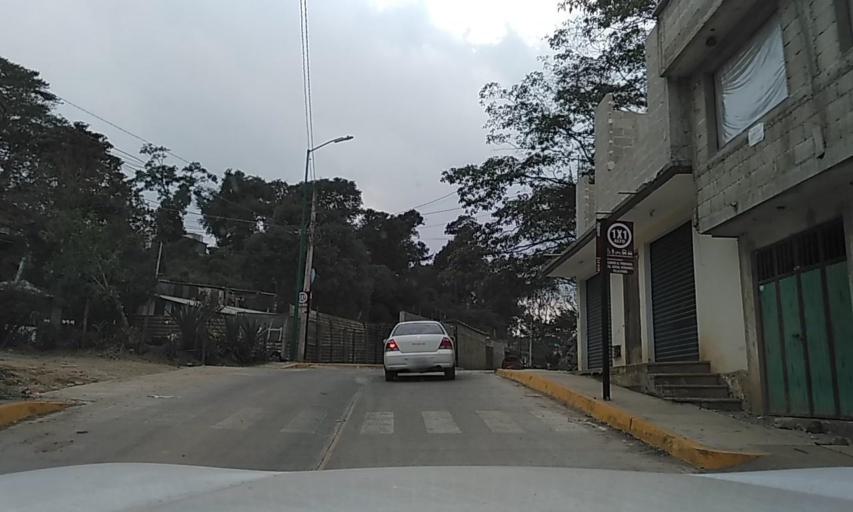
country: MX
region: Veracruz
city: El Castillo
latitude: 19.5710
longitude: -96.8933
